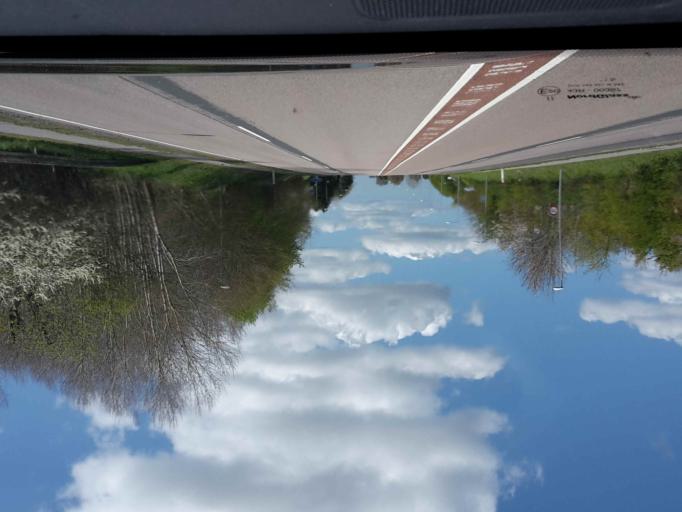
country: DK
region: South Denmark
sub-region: Assens Kommune
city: Tommerup
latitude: 55.3895
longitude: 10.2481
